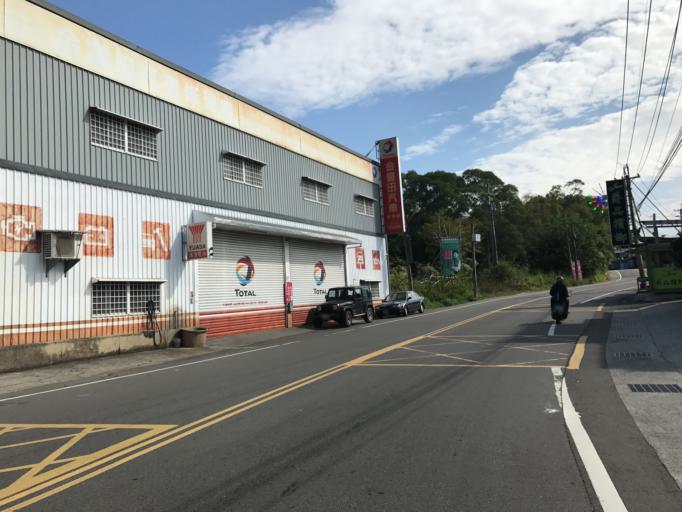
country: TW
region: Taiwan
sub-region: Hsinchu
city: Hsinchu
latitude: 24.7671
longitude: 120.9946
